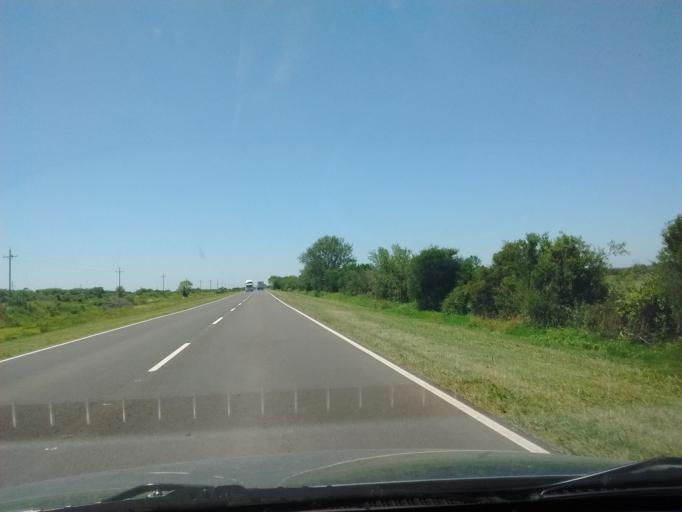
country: AR
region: Entre Rios
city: General Galarza
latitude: -32.8826
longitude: -59.7051
